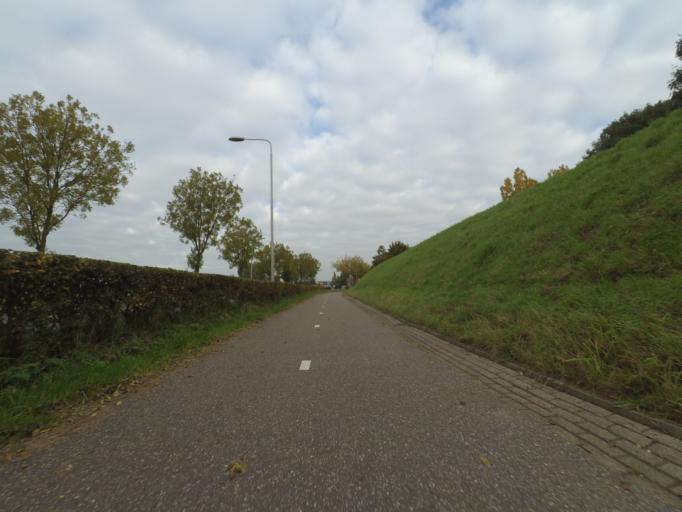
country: NL
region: Gelderland
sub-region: Gemeente Nijkerk
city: Nijkerk
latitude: 52.2254
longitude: 5.4701
